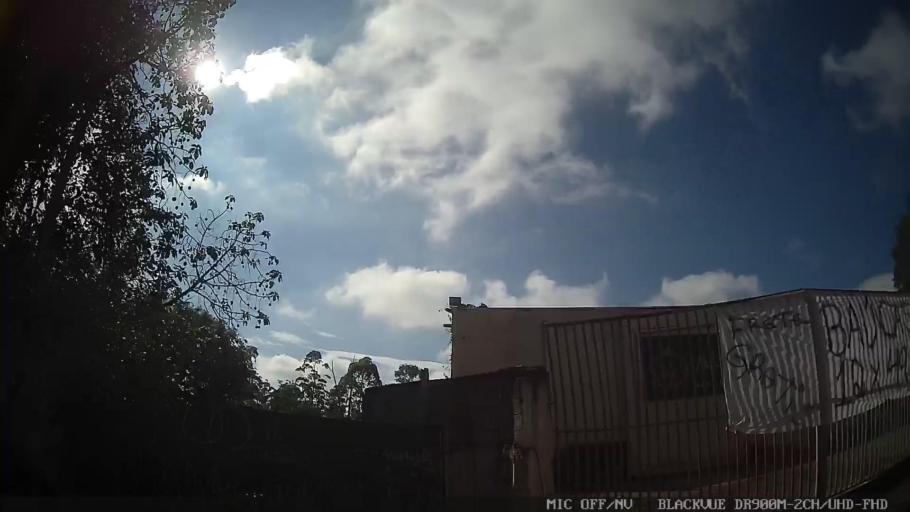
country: BR
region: Sao Paulo
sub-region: Itaquaquecetuba
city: Itaquaquecetuba
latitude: -23.4759
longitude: -46.3493
